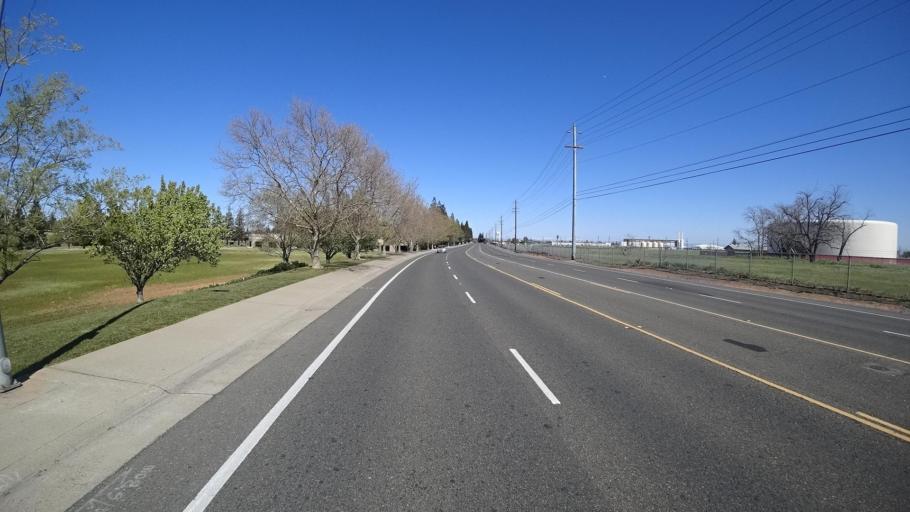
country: US
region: California
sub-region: Sacramento County
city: Rancho Cordova
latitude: 38.5621
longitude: -121.3152
